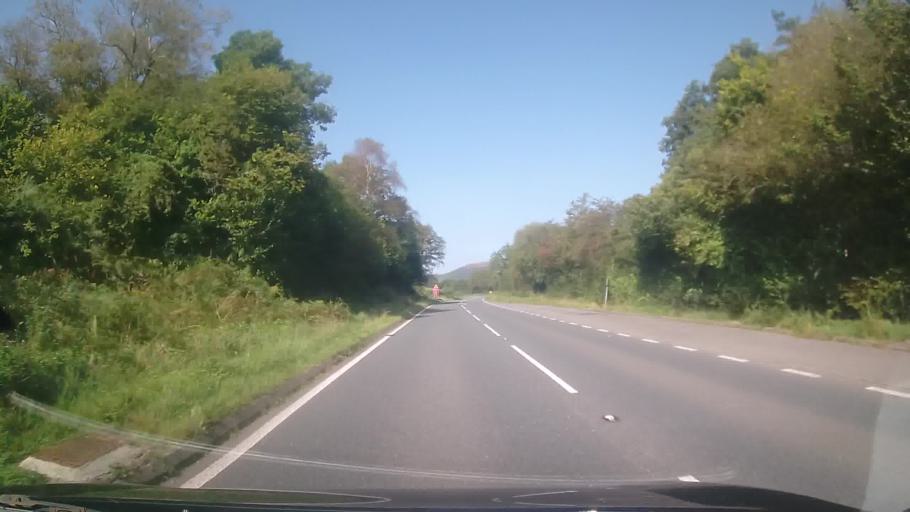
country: GB
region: Wales
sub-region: Sir Powys
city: Builth Wells
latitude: 52.1410
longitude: -3.5709
